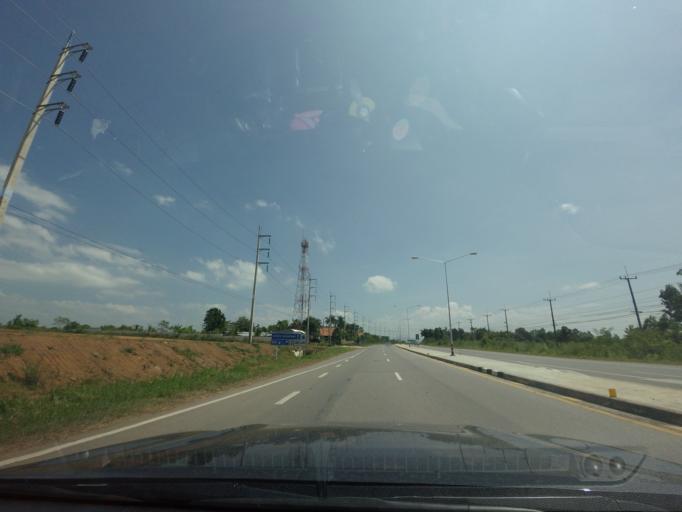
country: TH
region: Phetchabun
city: Lom Sak
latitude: 16.7682
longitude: 101.1799
